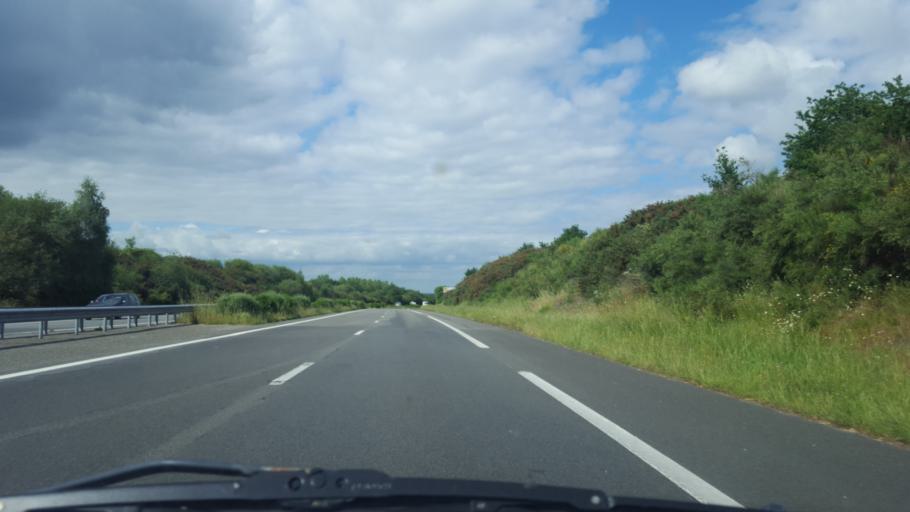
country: FR
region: Pays de la Loire
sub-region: Departement de la Loire-Atlantique
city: Saint-Philbert-de-Grand-Lieu
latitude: 47.0280
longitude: -1.6668
